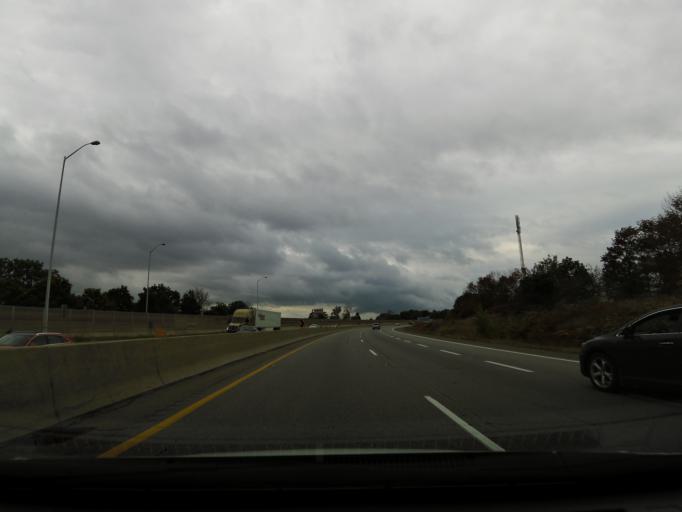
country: CA
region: Ontario
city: Brockville
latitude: 44.5302
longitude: -75.7676
